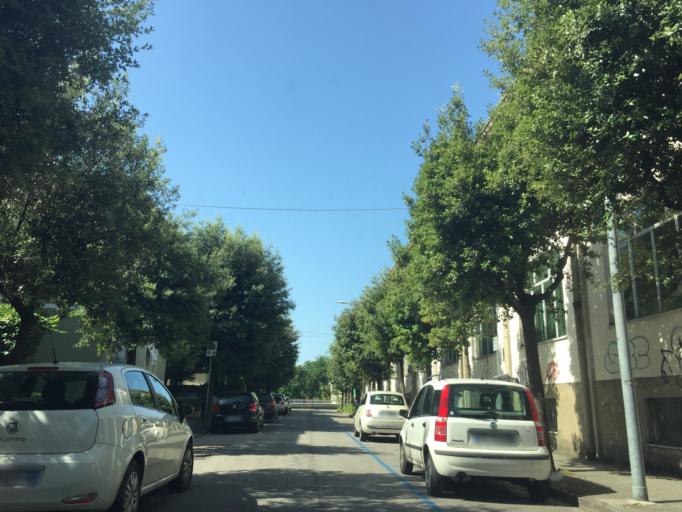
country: IT
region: Tuscany
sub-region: Province of Pisa
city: Pisa
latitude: 43.7203
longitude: 10.3883
